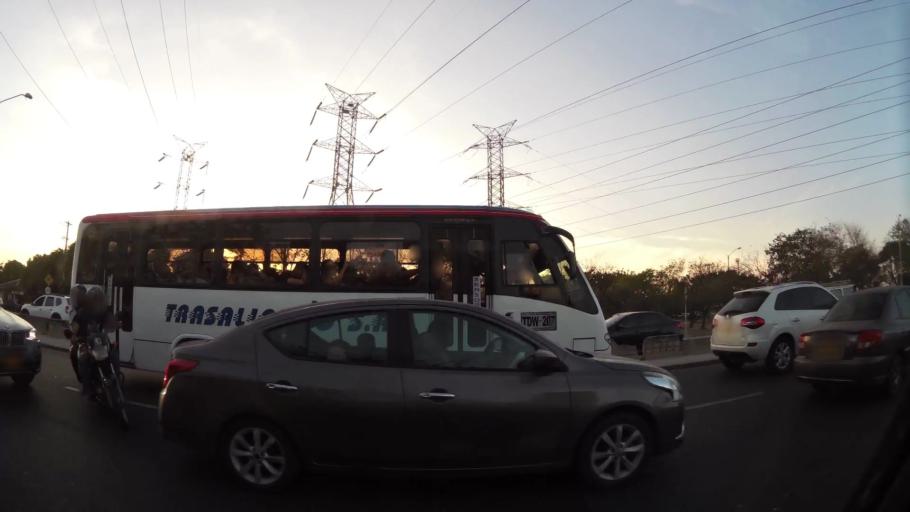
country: CO
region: Atlantico
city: Soledad
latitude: 10.9326
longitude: -74.7802
